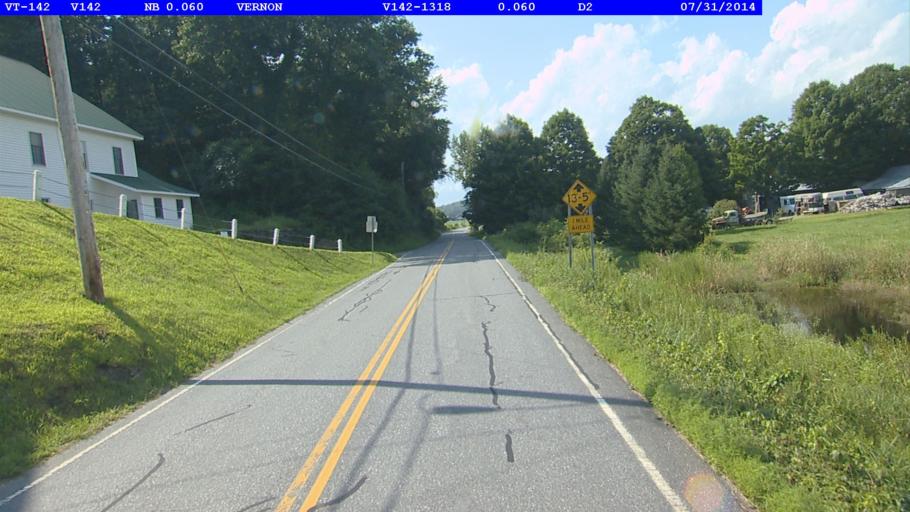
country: US
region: Massachusetts
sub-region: Franklin County
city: Northfield
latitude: 42.7278
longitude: -72.4654
